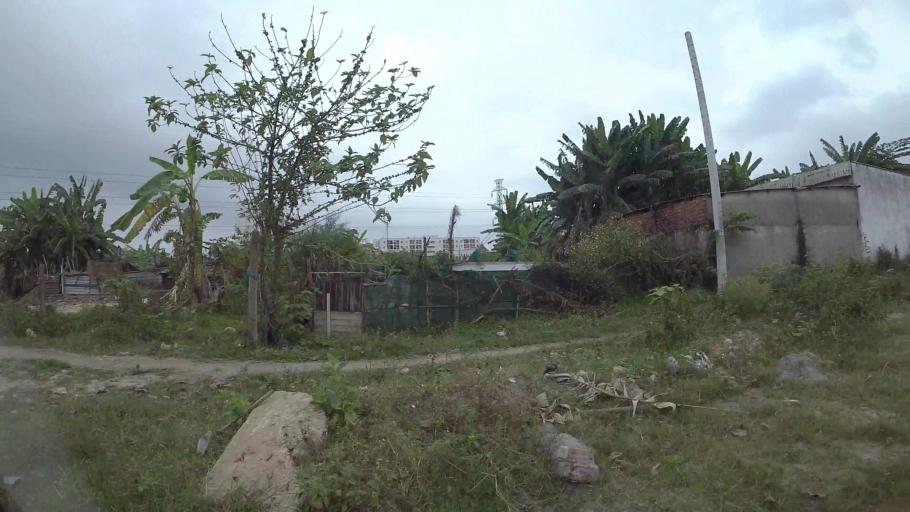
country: VN
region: Da Nang
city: Lien Chieu
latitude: 16.0442
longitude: 108.1725
